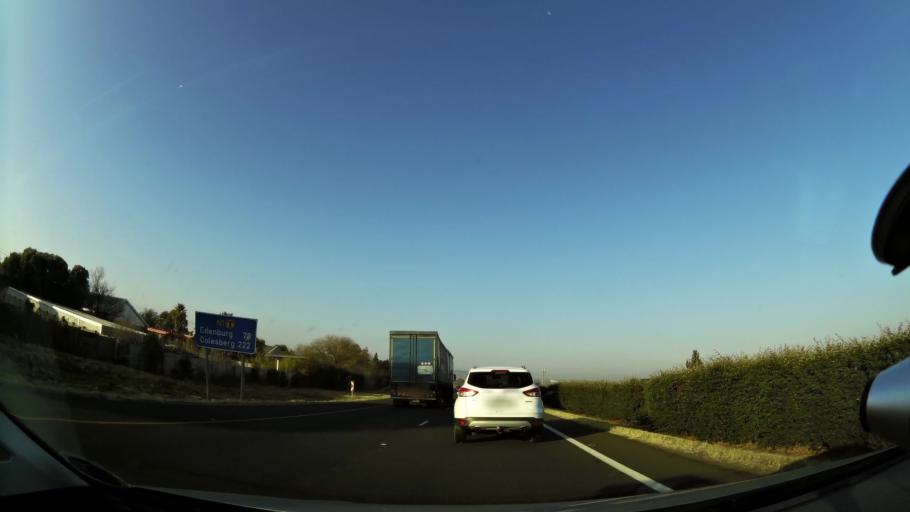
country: ZA
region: Orange Free State
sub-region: Mangaung Metropolitan Municipality
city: Bloemfontein
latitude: -29.1004
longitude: 26.1653
